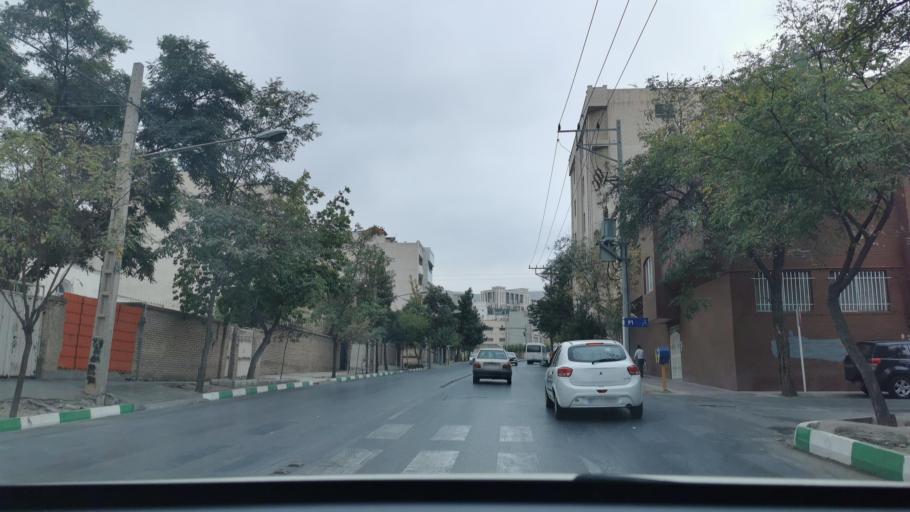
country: IR
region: Razavi Khorasan
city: Mashhad
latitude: 36.3069
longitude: 59.5013
